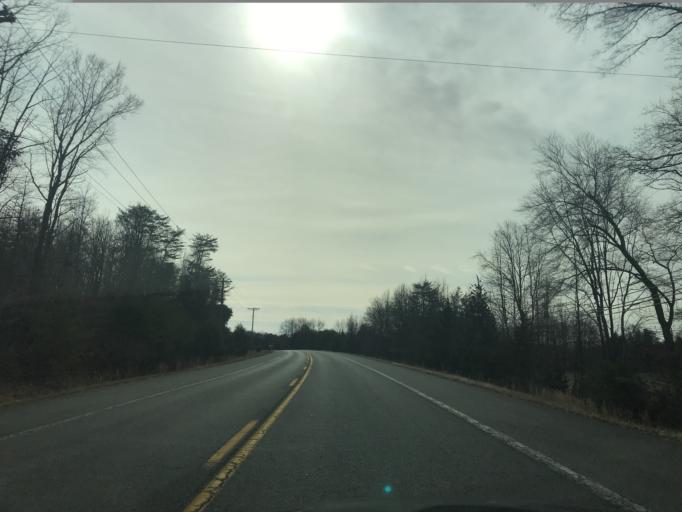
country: US
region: Virginia
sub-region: Prince William County
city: Cherry Hill
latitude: 38.4798
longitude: -77.2285
